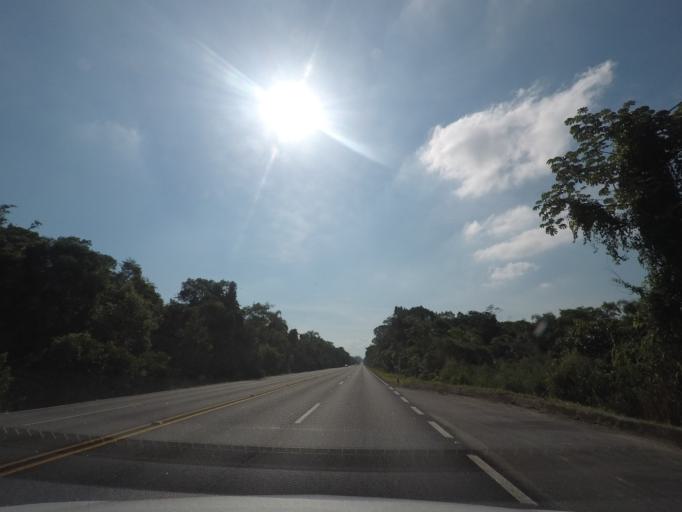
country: BR
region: Parana
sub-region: Pontal Do Parana
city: Pontal do Parana
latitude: -25.6242
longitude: -48.5982
